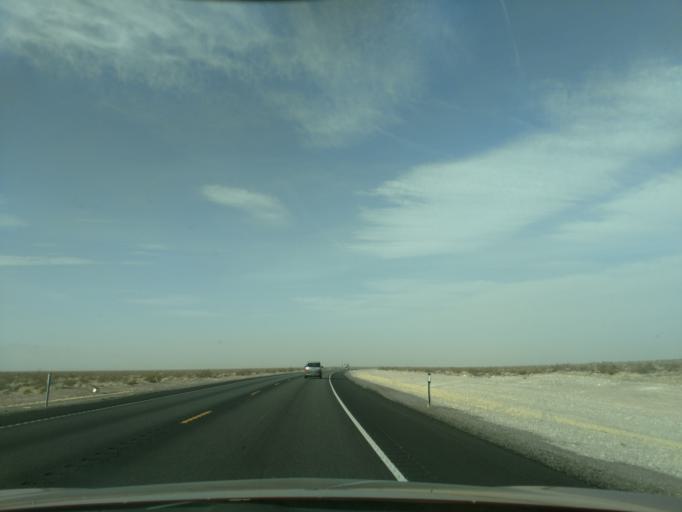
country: US
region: Nevada
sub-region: Nye County
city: Beatty
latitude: 36.6317
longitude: -116.3493
